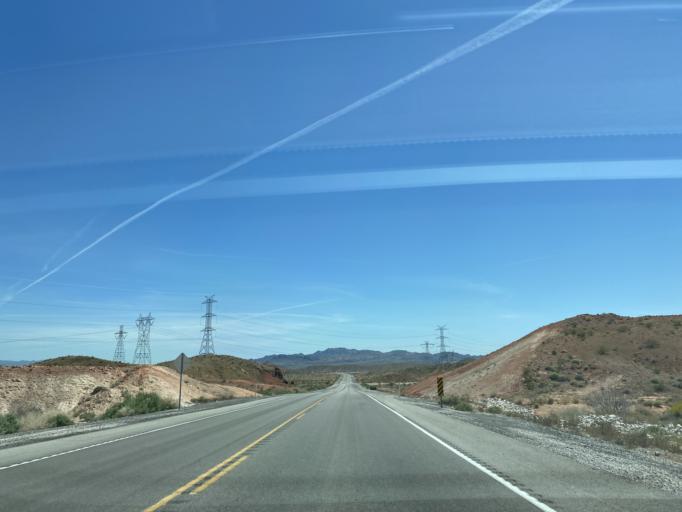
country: US
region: Nevada
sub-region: Clark County
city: Nellis Air Force Base
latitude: 36.1894
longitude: -114.9198
